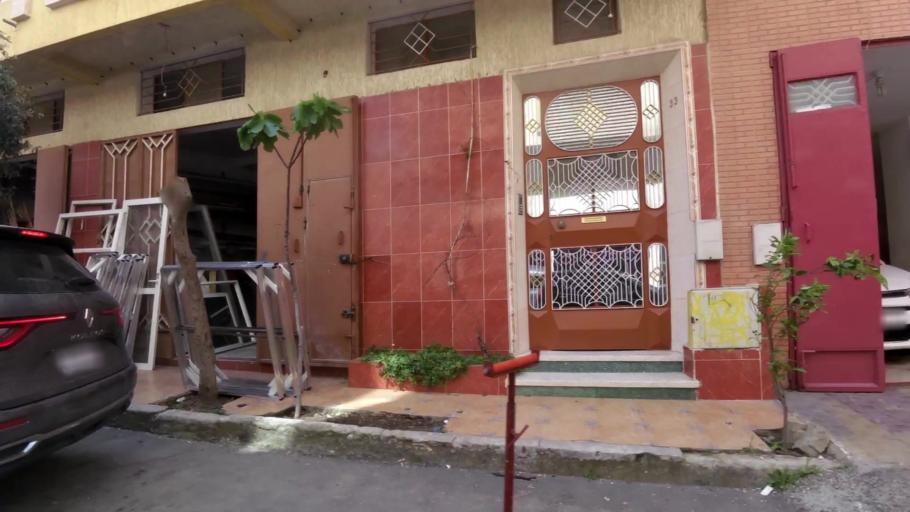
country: MA
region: Tanger-Tetouan
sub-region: Tanger-Assilah
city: Tangier
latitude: 35.7390
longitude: -5.8328
